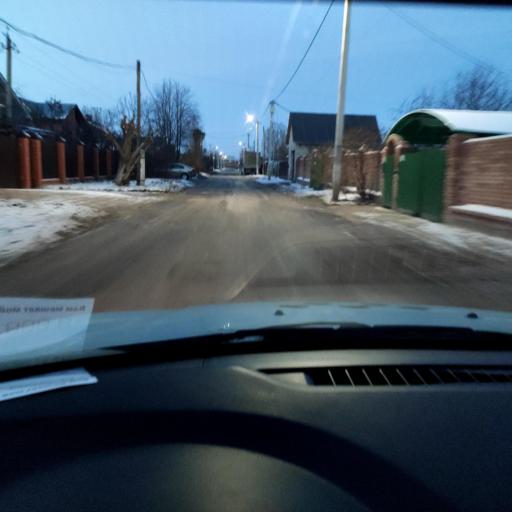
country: RU
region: Samara
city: Tol'yatti
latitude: 53.5654
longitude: 49.3899
